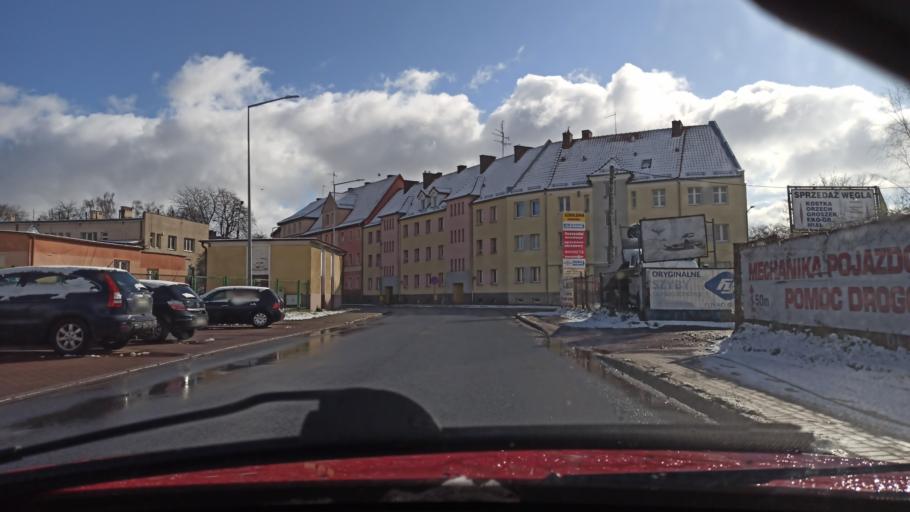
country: PL
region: Warmian-Masurian Voivodeship
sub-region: Powiat elblaski
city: Elblag
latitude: 54.1525
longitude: 19.3991
